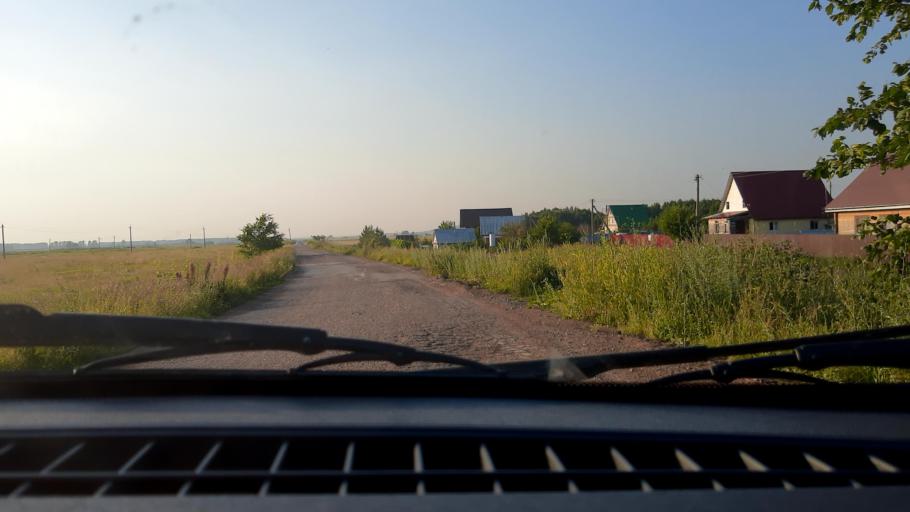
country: RU
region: Bashkortostan
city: Asanovo
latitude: 54.9160
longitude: 55.6273
